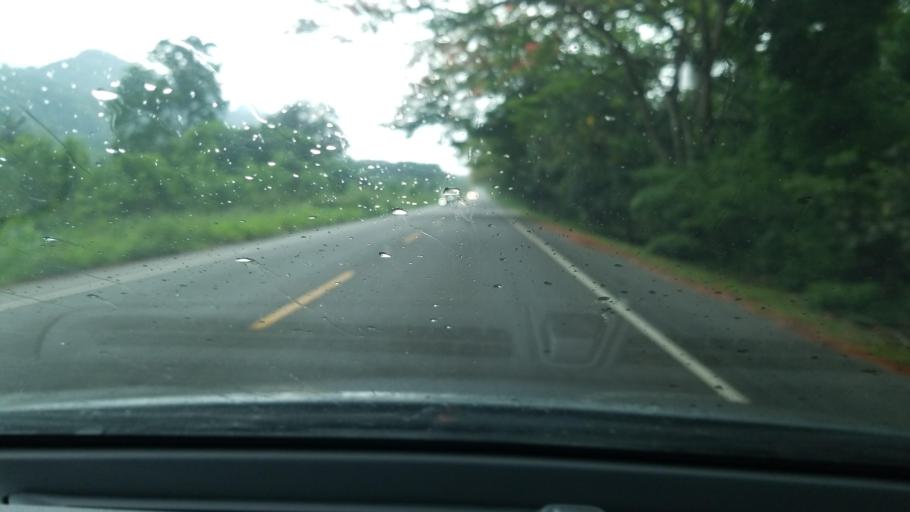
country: HN
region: Cortes
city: Rio Chiquito
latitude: 15.6211
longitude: -88.2666
